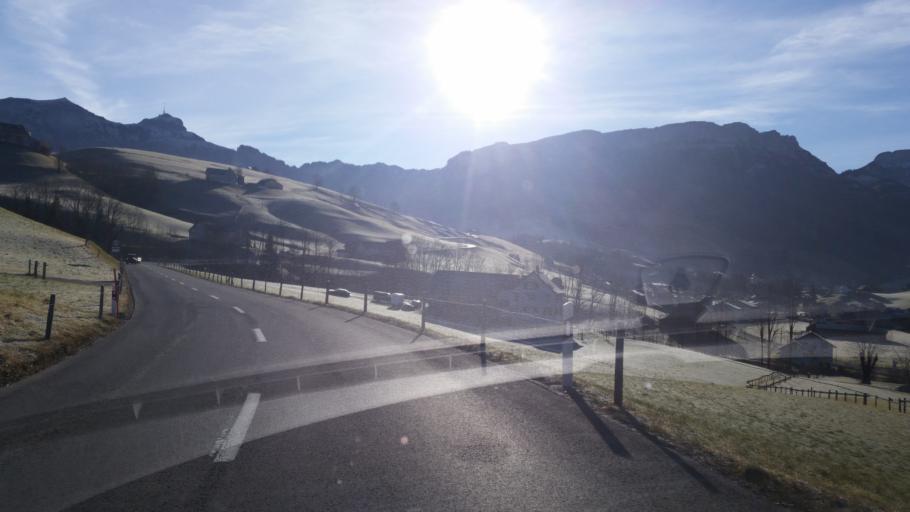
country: CH
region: Appenzell Innerrhoden
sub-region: Appenzell Inner Rhodes
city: Appenzell
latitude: 47.3169
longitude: 9.4356
